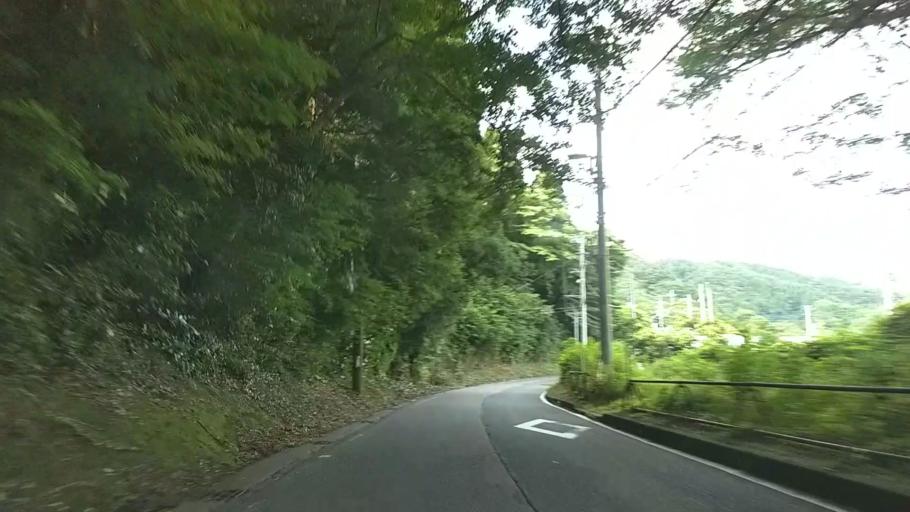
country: JP
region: Yamanashi
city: Uenohara
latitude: 35.6049
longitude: 139.1553
